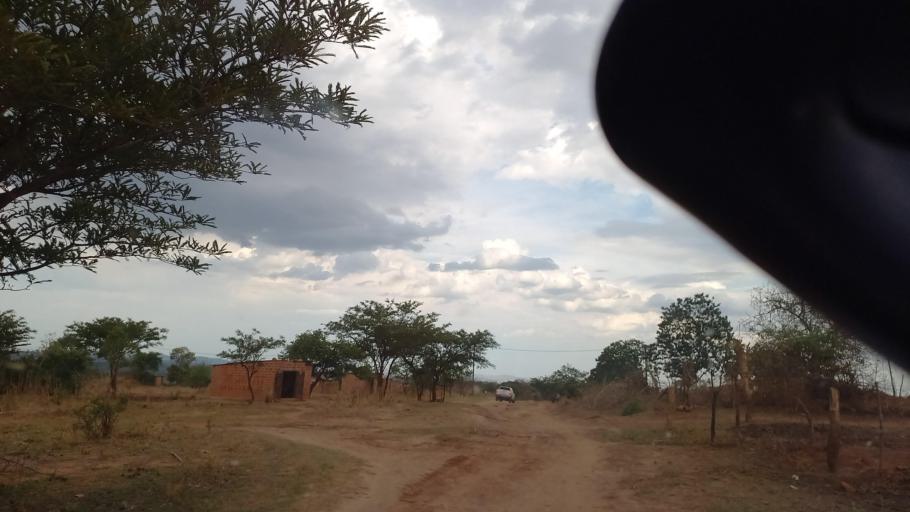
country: ZM
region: Lusaka
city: Kafue
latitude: -16.1354
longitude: 28.0533
